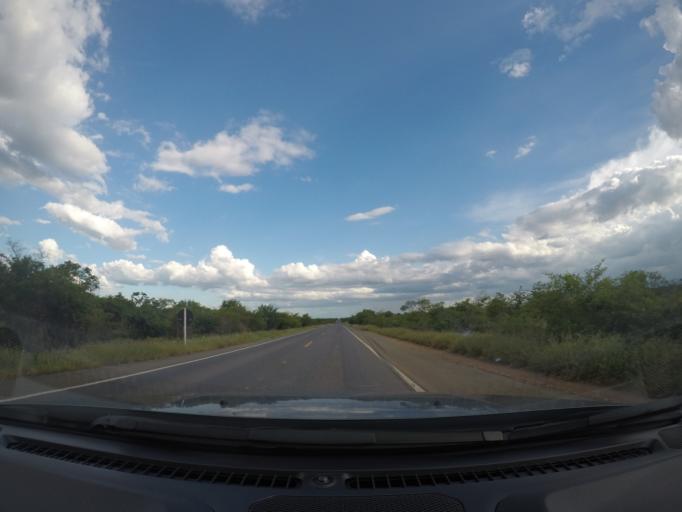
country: BR
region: Bahia
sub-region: Oliveira Dos Brejinhos
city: Beira Rio
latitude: -12.1931
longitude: -42.8211
